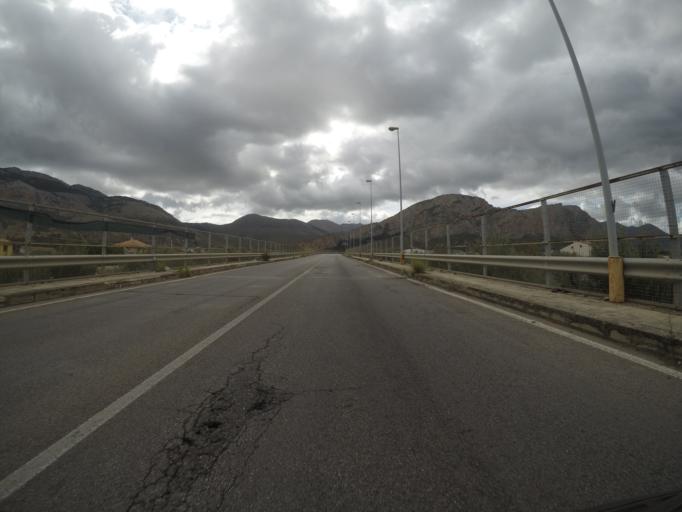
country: IT
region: Sicily
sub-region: Palermo
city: Capaci
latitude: 38.1692
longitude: 13.2213
